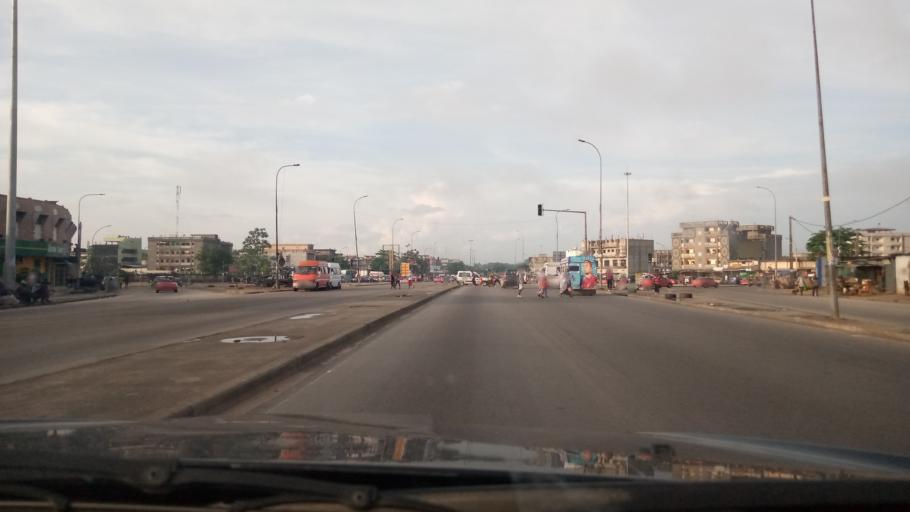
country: CI
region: Lagunes
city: Abobo
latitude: 5.4128
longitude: -4.0161
